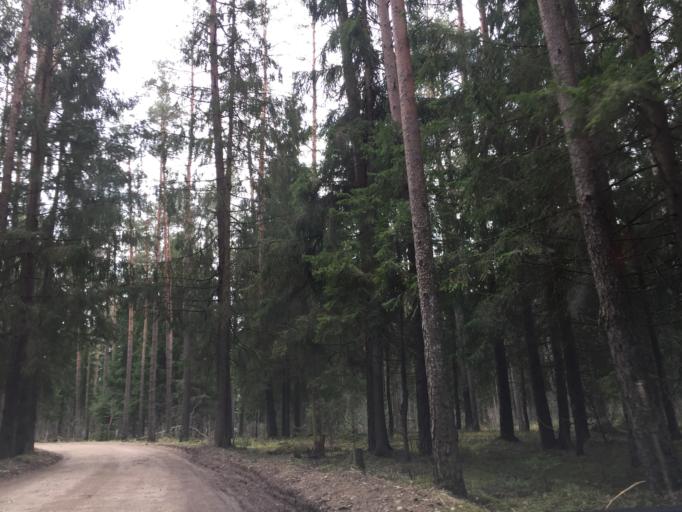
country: LV
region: Incukalns
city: Vangazi
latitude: 57.0979
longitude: 24.5435
